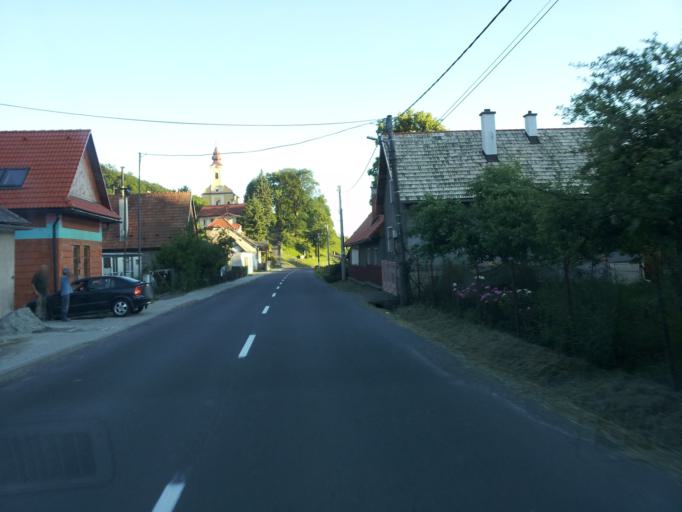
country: SK
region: Banskobystricky
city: Svaety Anton
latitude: 48.4211
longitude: 18.9410
